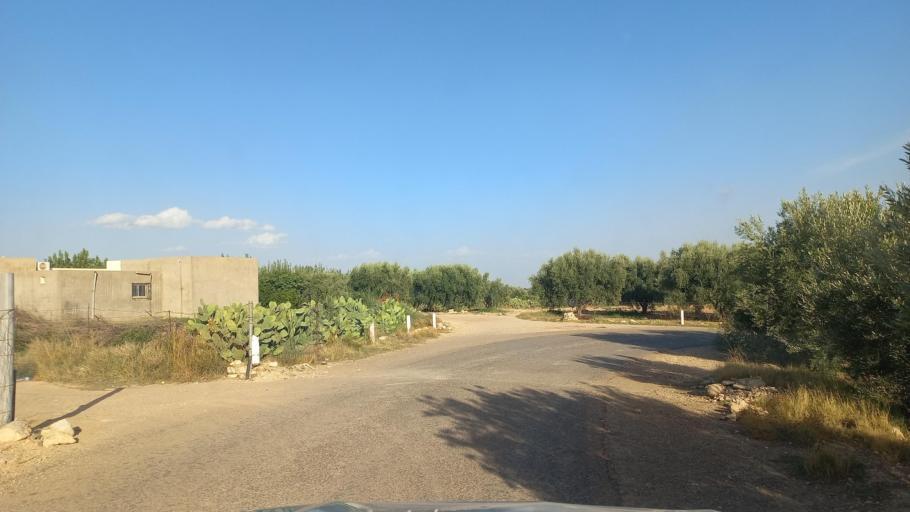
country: TN
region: Al Qasrayn
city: Kasserine
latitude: 35.2729
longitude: 9.0306
